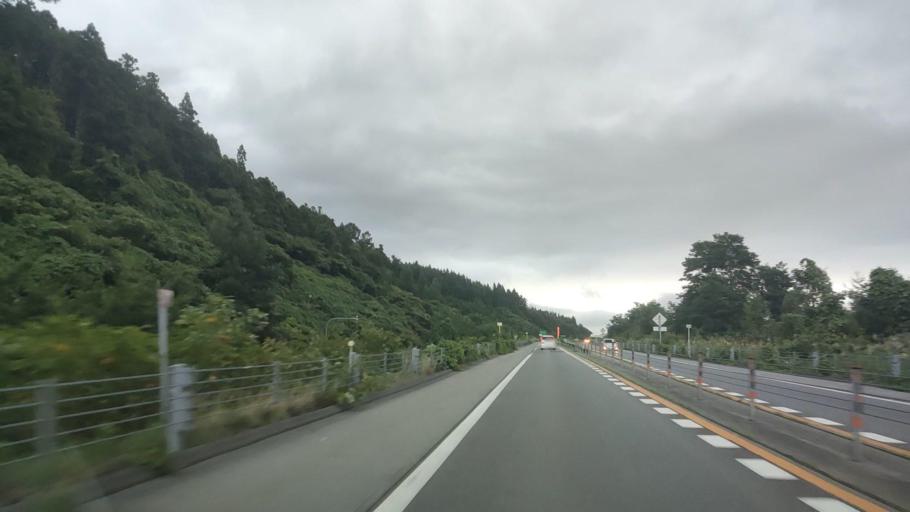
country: JP
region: Hokkaido
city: Nanae
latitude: 41.9102
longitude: 140.6940
